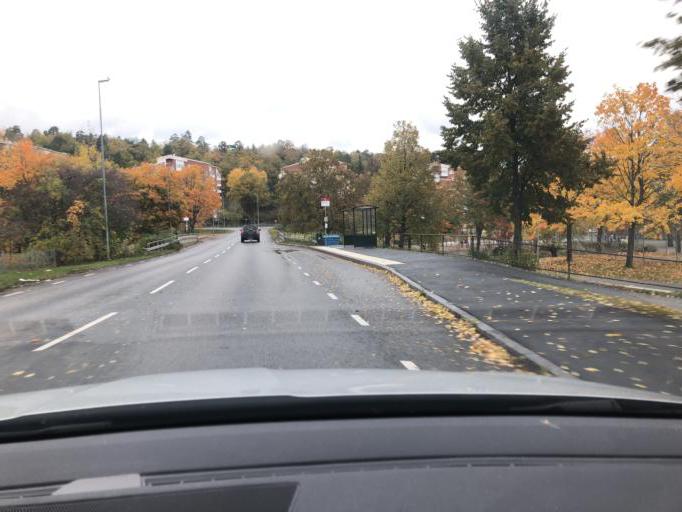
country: SE
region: Stockholm
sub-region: Botkyrka Kommun
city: Alby
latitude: 59.2371
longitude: 17.8519
